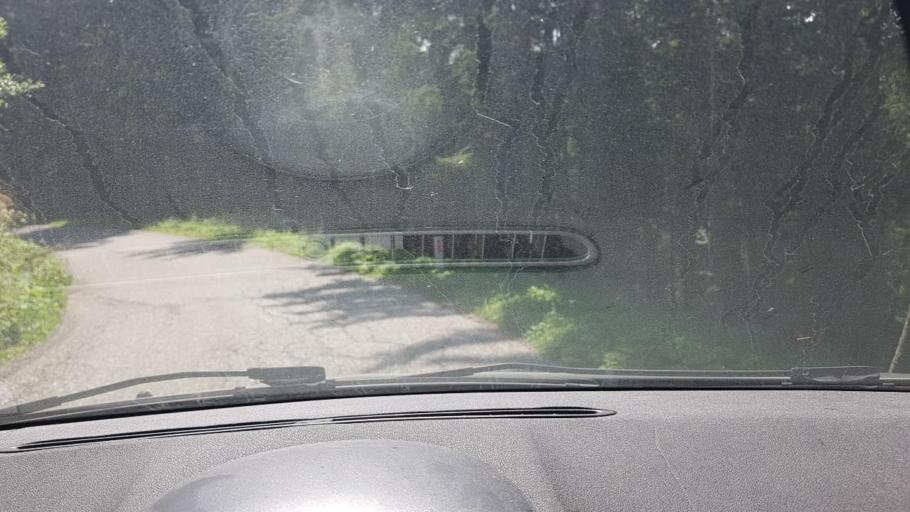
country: AT
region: Carinthia
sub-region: Politischer Bezirk Volkermarkt
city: Bad Eisenkappel
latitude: 46.4237
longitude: 14.5709
